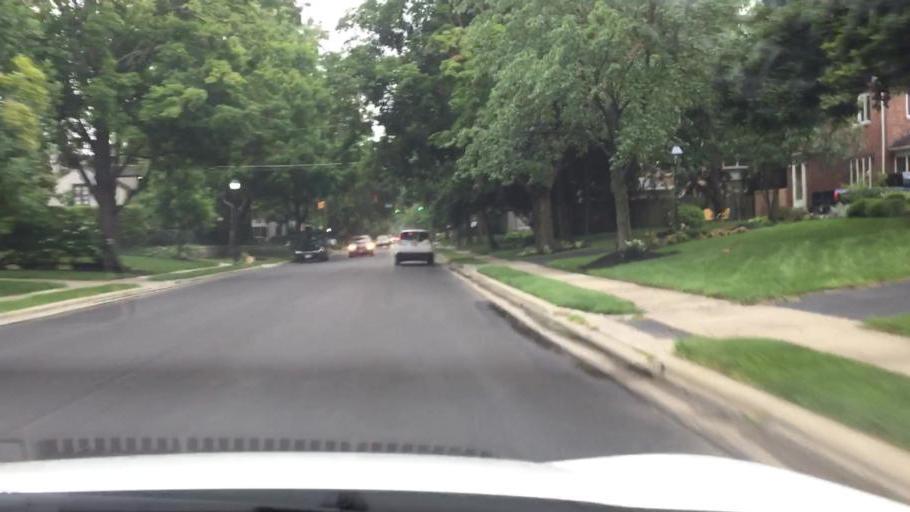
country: US
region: Ohio
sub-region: Franklin County
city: Bexley
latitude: 39.9628
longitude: -82.9270
